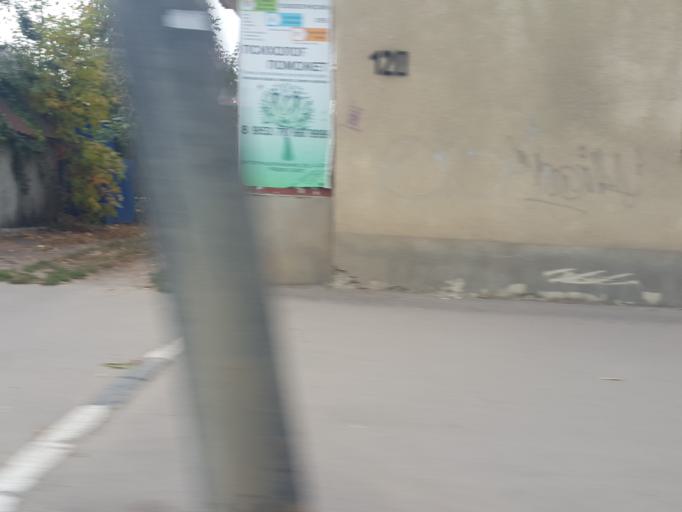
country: RU
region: Tambov
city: Tambov
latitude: 52.7261
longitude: 41.4437
